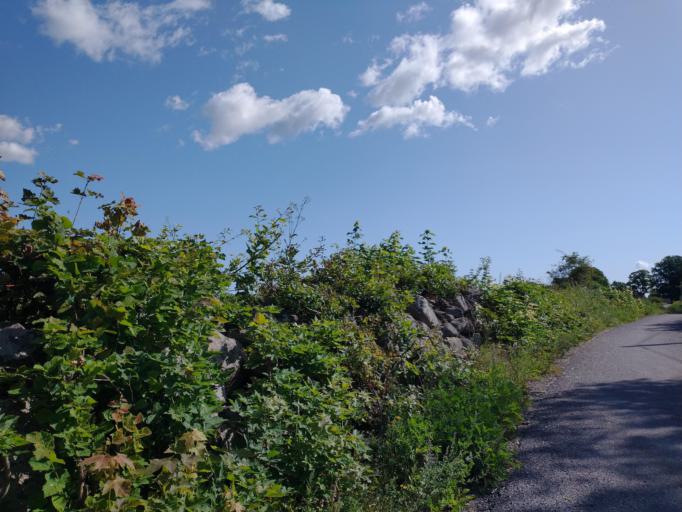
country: SE
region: Kalmar
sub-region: Kalmar Kommun
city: Lindsdal
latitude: 56.7936
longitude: 16.2851
